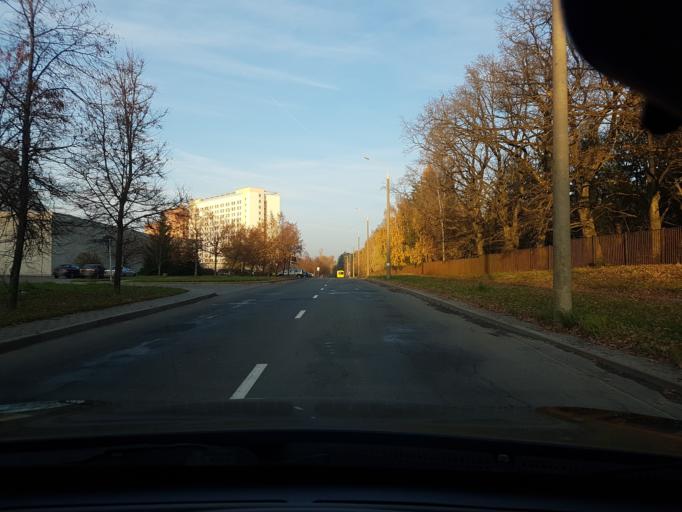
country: BY
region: Minsk
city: Shchomyslitsa
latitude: 53.8356
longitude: 27.4683
